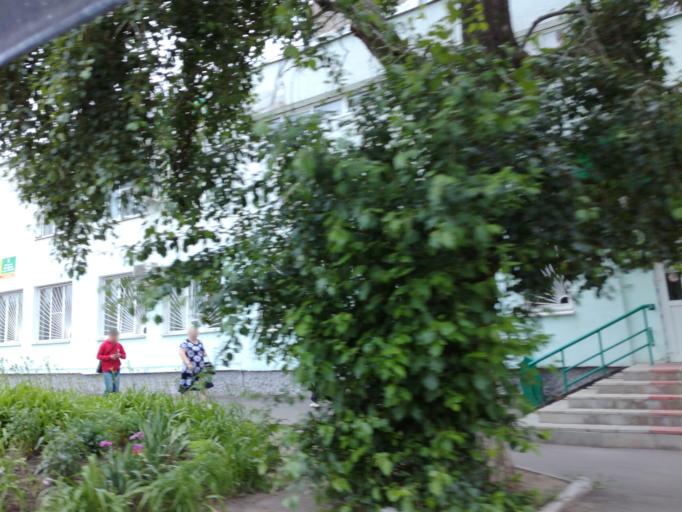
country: RU
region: Kursk
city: Kursk
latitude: 51.7245
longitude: 36.1687
